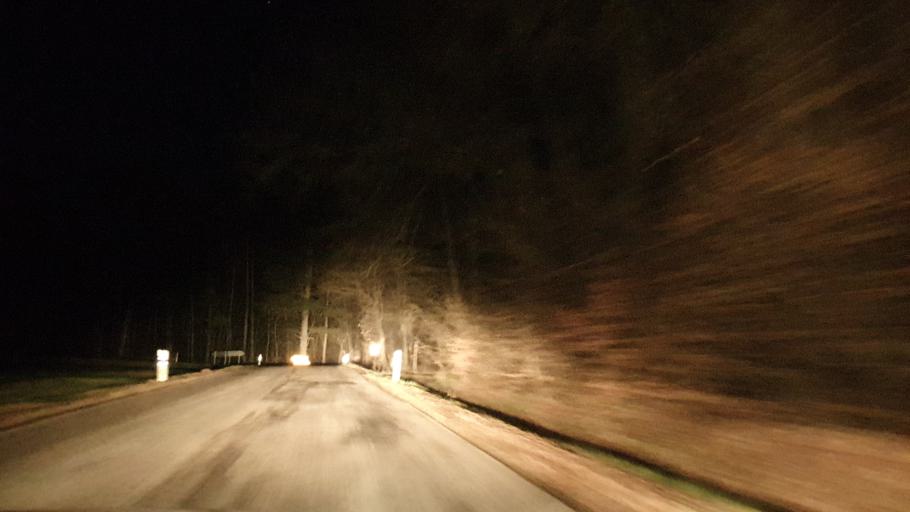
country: DE
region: Rheinland-Pfalz
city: Oberdreis
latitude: 50.6352
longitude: 7.6511
